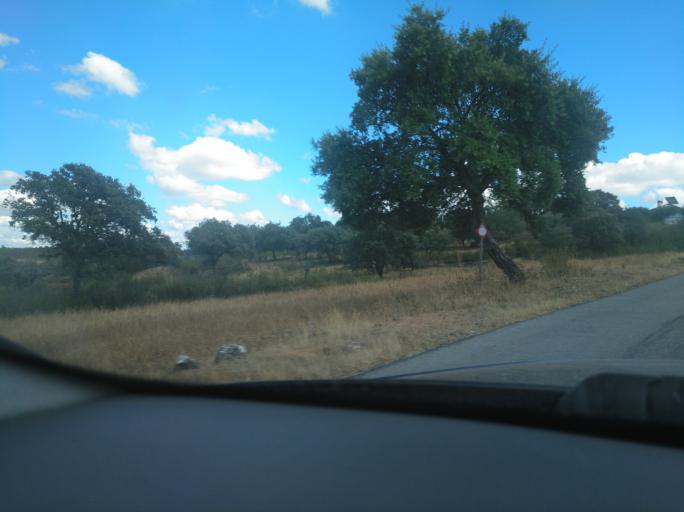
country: ES
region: Extremadura
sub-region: Provincia de Badajoz
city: La Codosera
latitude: 39.1490
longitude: -7.1580
